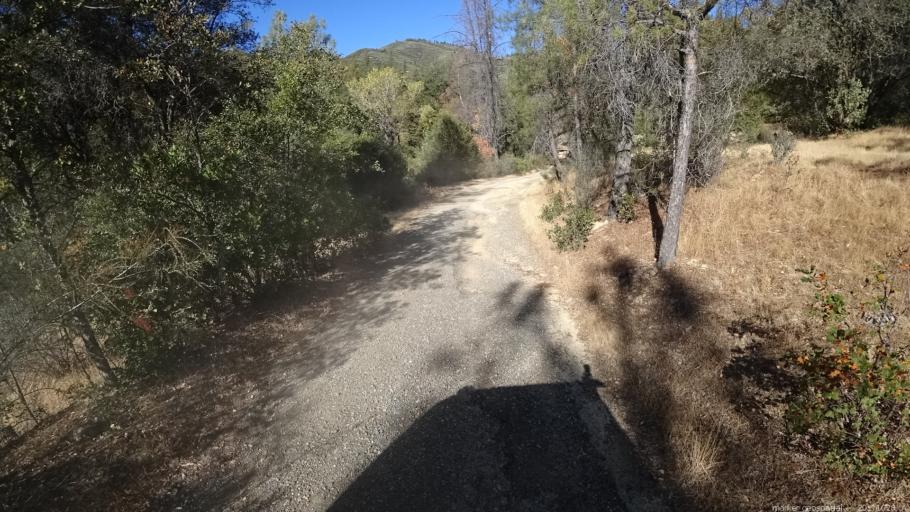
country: US
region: California
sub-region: Shasta County
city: Shasta
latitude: 40.6564
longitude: -122.5988
